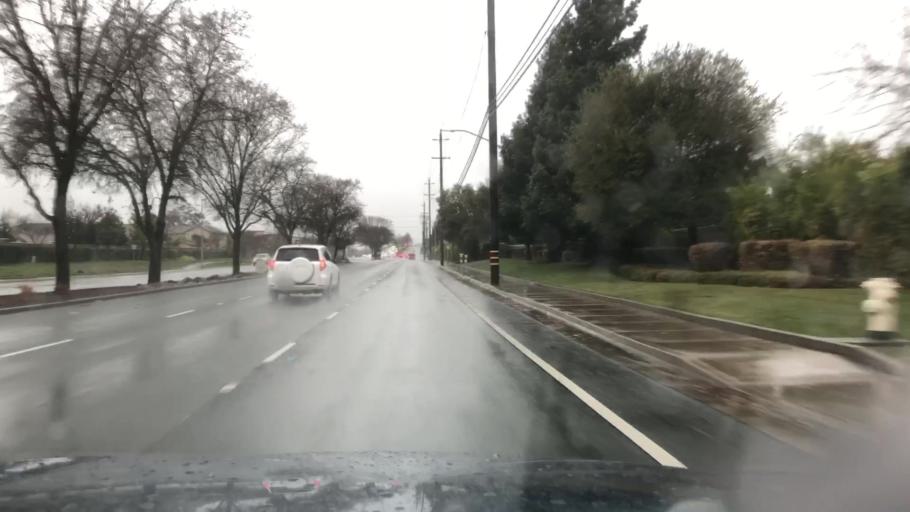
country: US
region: California
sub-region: Sacramento County
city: Laguna
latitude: 38.4088
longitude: -121.4449
